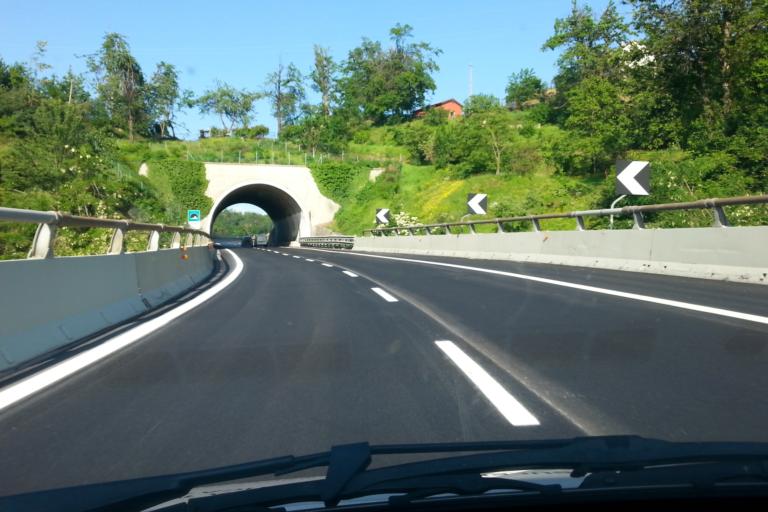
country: IT
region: Liguria
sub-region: Provincia di Savona
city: Altare
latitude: 44.3343
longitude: 8.3367
